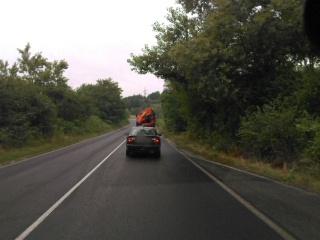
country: BG
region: Plovdiv
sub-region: Obshtina Karlovo
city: Karlovo
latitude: 42.5356
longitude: 24.8172
